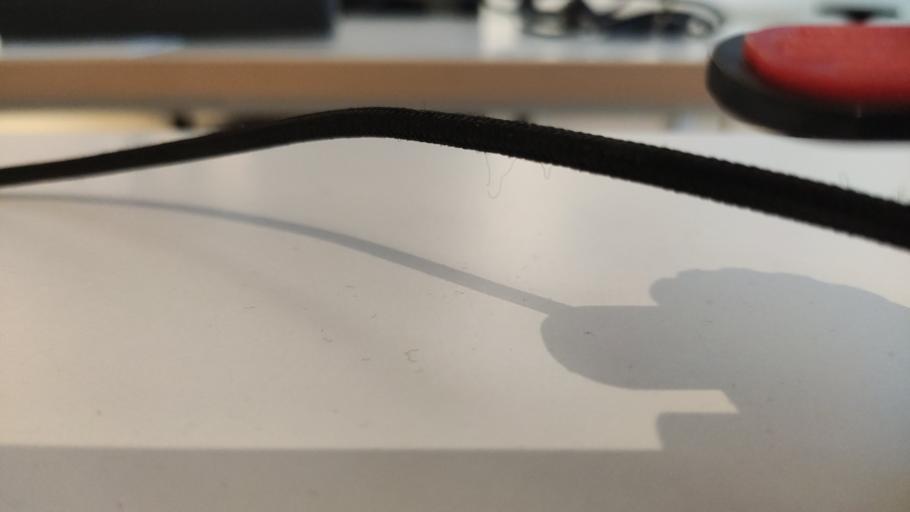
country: RU
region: Moskovskaya
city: Novopetrovskoye
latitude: 55.8602
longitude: 36.3832
